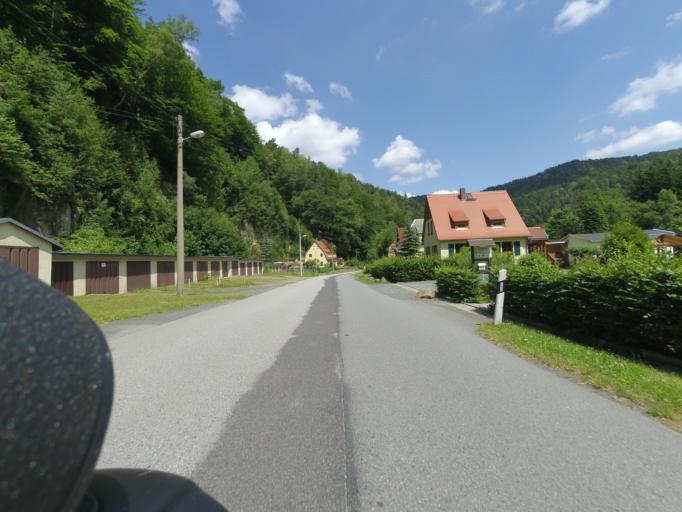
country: DE
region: Saxony
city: Porschdorf
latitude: 50.9413
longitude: 14.1332
